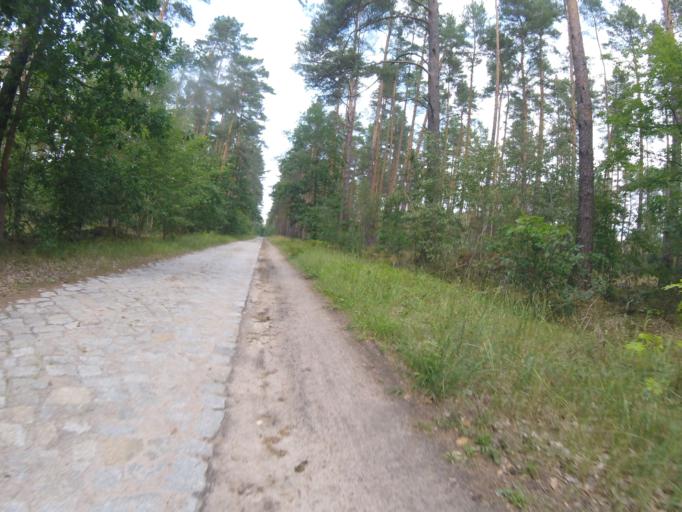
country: DE
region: Brandenburg
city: Schwerin
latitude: 52.1801
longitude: 13.5965
